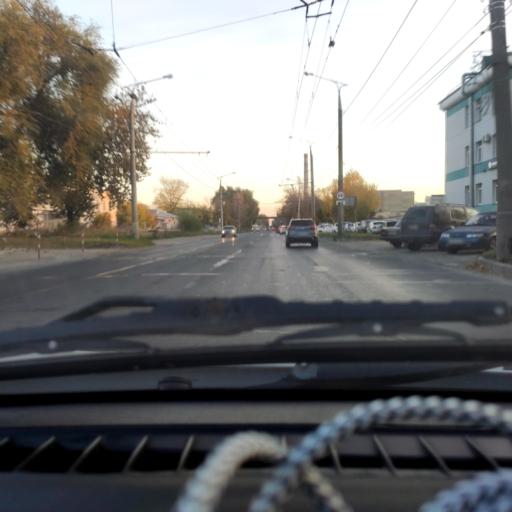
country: RU
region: Samara
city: Tol'yatti
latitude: 53.5414
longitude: 49.4437
